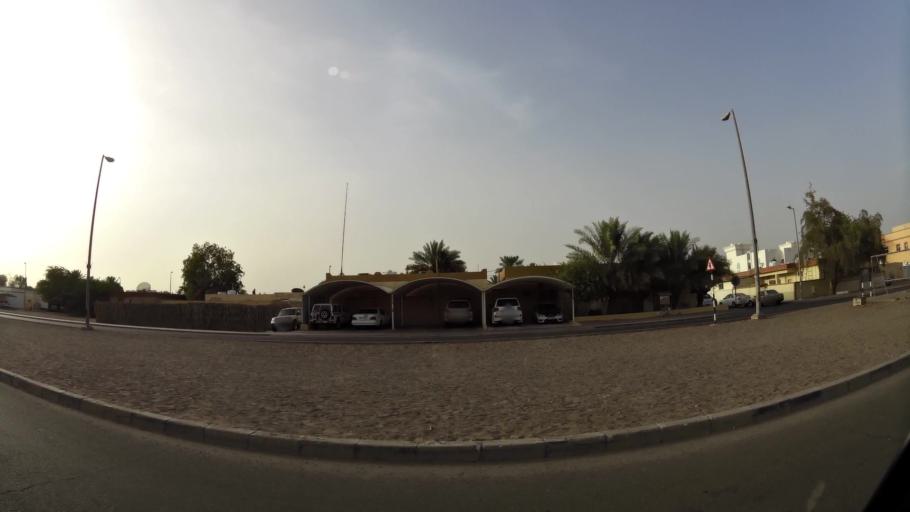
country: OM
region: Al Buraimi
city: Al Buraymi
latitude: 24.2423
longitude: 55.7498
